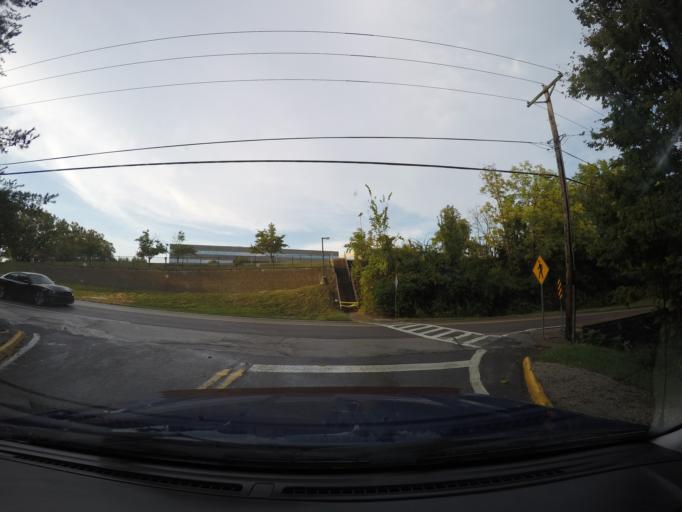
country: US
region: Missouri
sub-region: Saint Louis County
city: Sunset Hills
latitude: 38.5518
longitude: -90.4151
